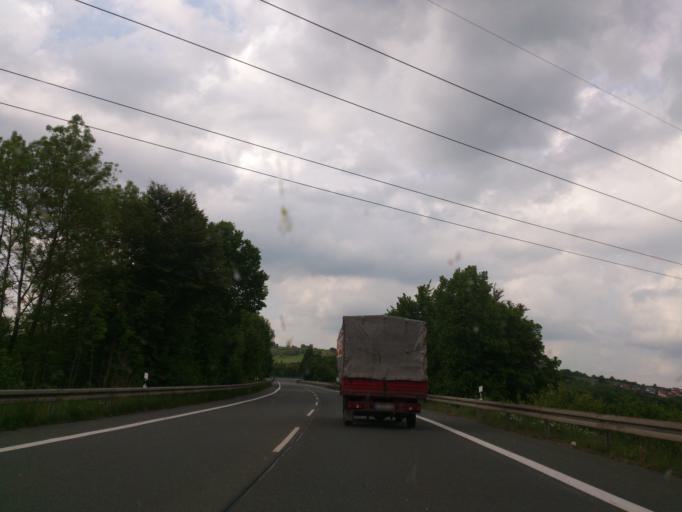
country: DE
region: North Rhine-Westphalia
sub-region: Regierungsbezirk Detmold
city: Willebadessen
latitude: 51.5174
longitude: 9.0126
